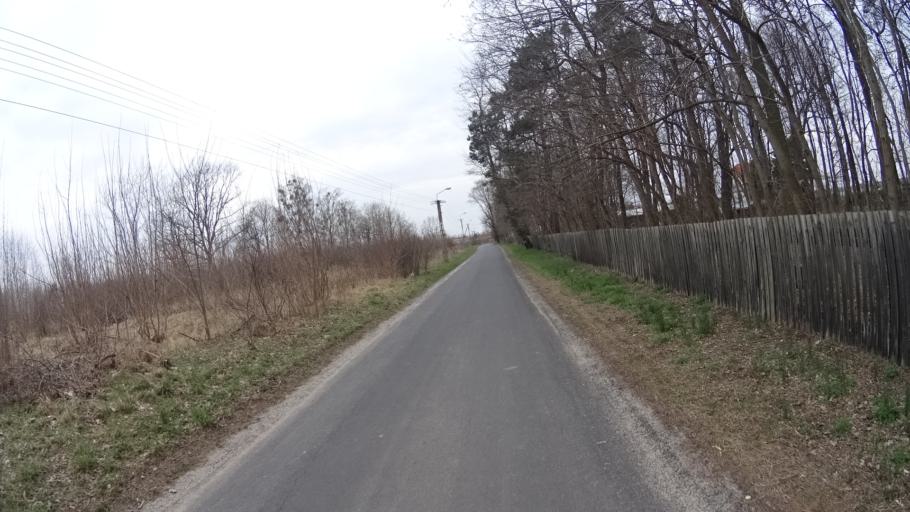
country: PL
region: Masovian Voivodeship
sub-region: Powiat warszawski zachodni
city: Jozefow
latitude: 52.2471
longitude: 20.6681
